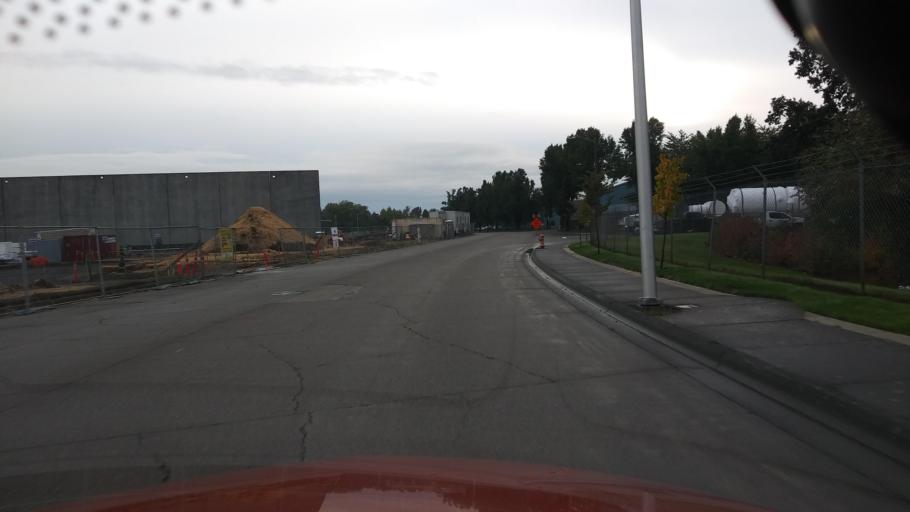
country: US
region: Oregon
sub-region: Washington County
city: Cornelius
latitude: 45.5268
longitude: -123.0637
